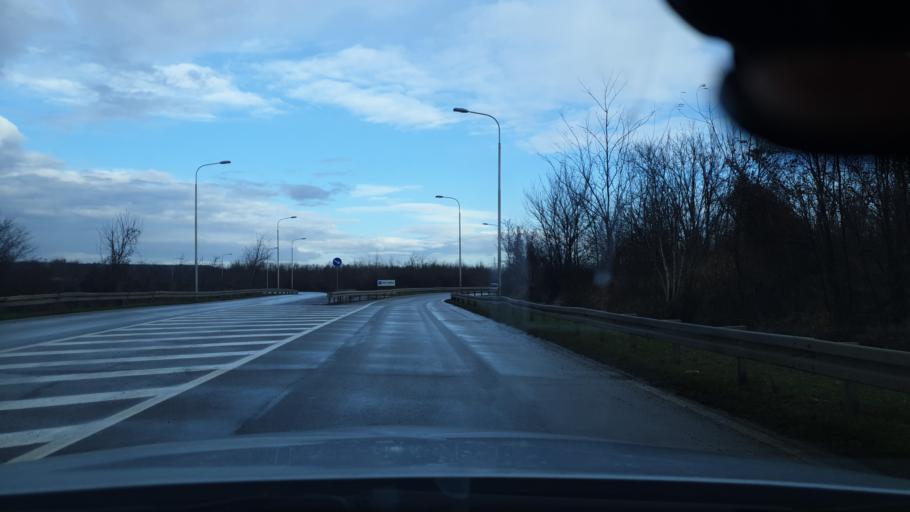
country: RS
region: Central Serbia
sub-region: Podunavski Okrug
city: Smederevo
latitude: 44.6065
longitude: 20.9550
